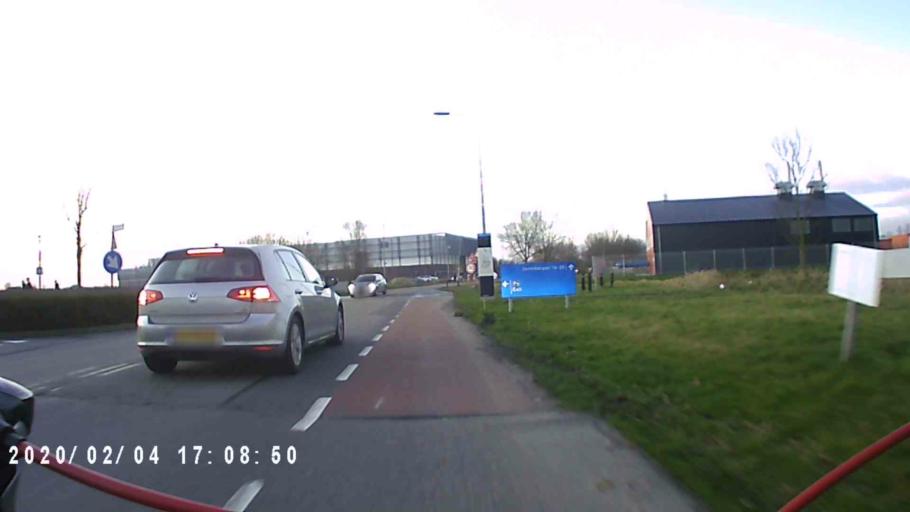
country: NL
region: Groningen
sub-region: Gemeente Groningen
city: Korrewegwijk
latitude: 53.2449
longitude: 6.5304
